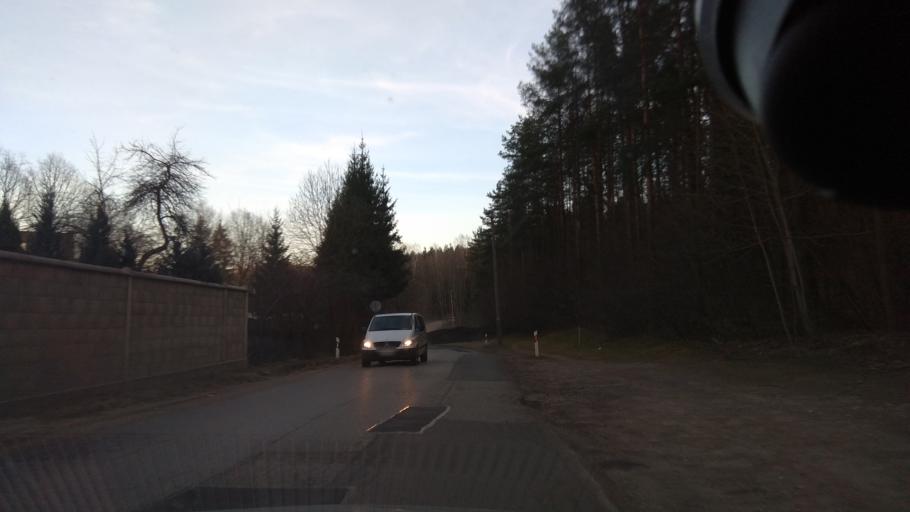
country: LT
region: Vilnius County
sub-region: Vilnius
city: Fabijoniskes
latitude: 54.7536
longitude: 25.2528
